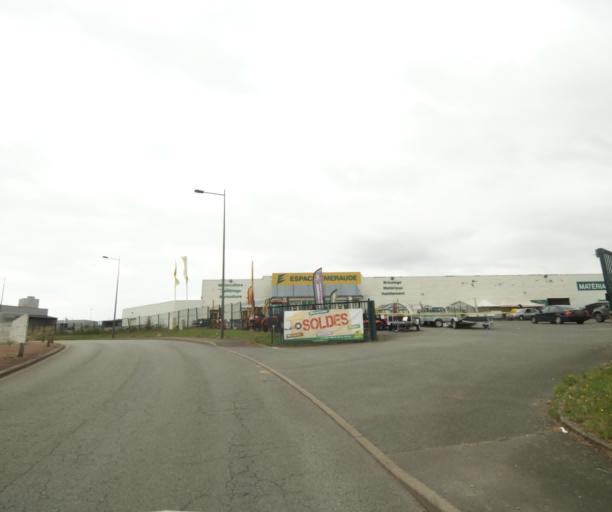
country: FR
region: Pays de la Loire
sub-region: Departement de la Sarthe
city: Solesmes
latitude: 47.8355
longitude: -0.3035
